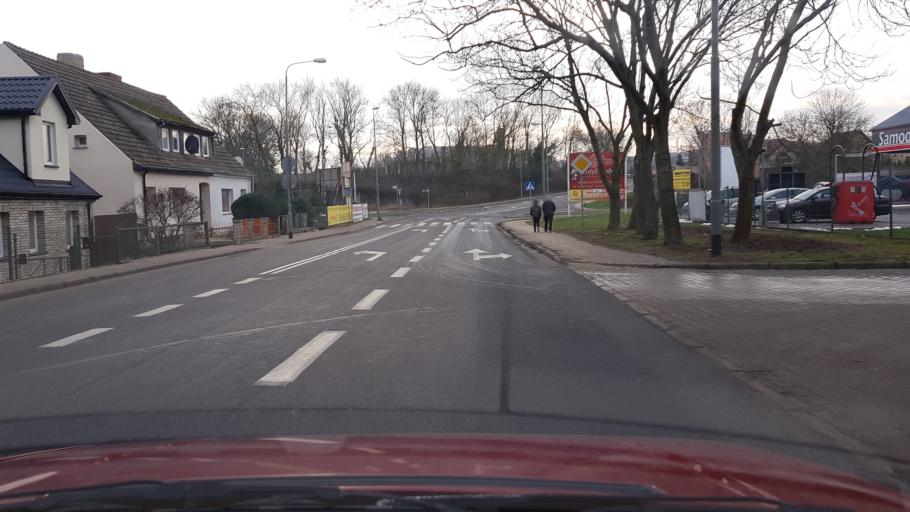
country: PL
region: West Pomeranian Voivodeship
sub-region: Powiat policki
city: Police
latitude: 53.5453
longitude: 14.5749
